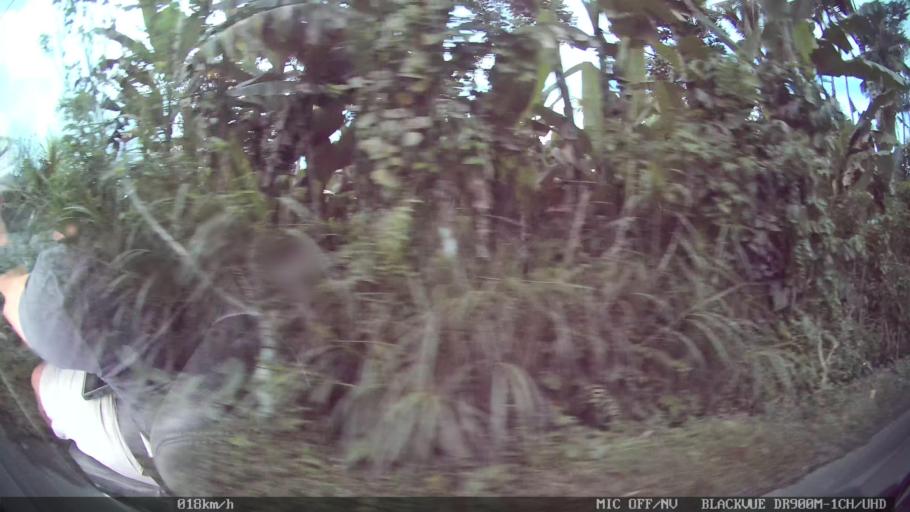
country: ID
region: Bali
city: Banjar Petak
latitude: -8.4458
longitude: 115.3227
